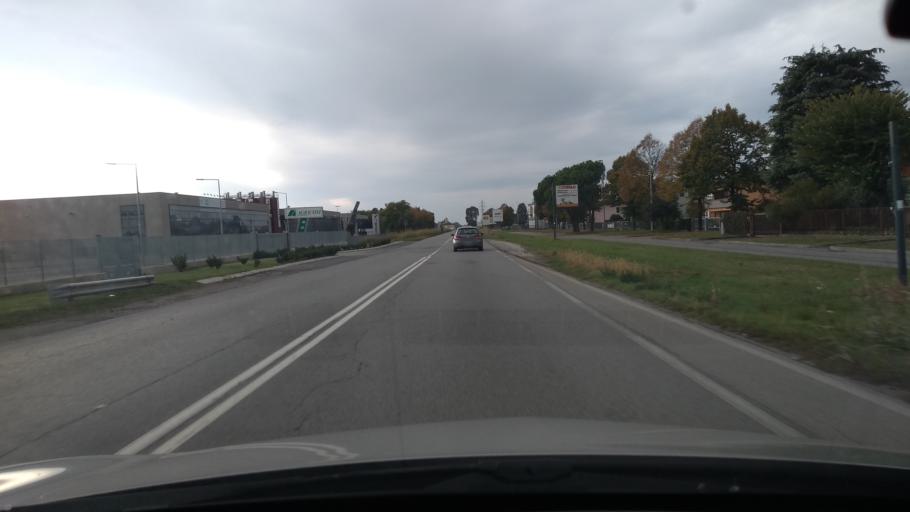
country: IT
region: Lombardy
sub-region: Provincia di Bergamo
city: Pognano
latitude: 45.5932
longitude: 9.6468
